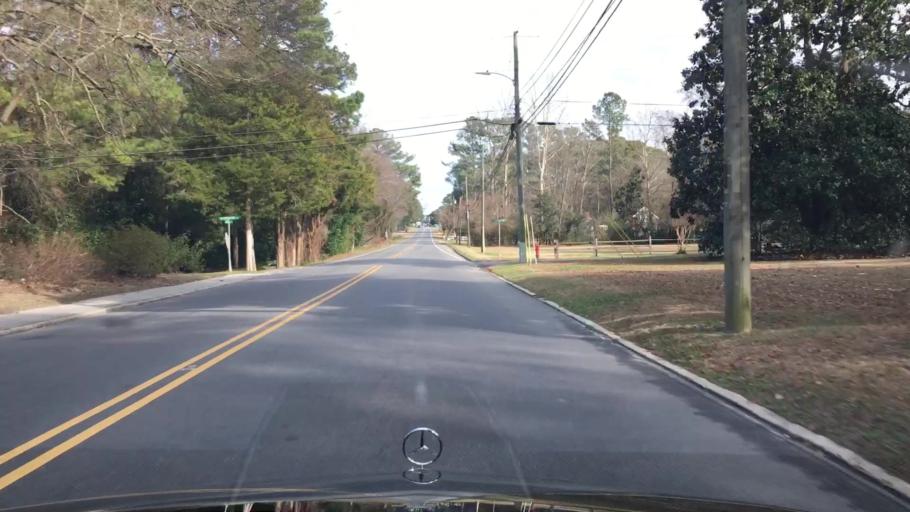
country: US
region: North Carolina
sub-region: Duplin County
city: Warsaw
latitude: 35.0008
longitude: -78.0861
